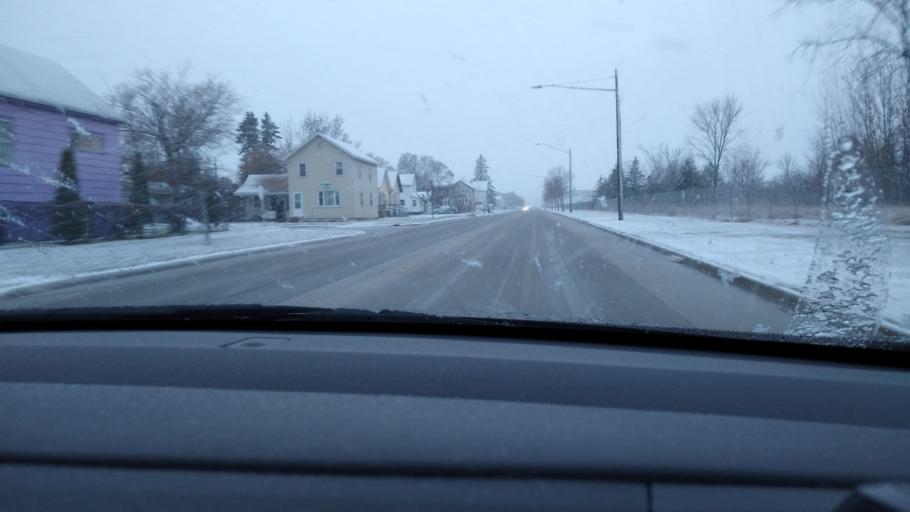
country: US
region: Michigan
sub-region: Delta County
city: Escanaba
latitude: 45.7494
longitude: -87.0621
